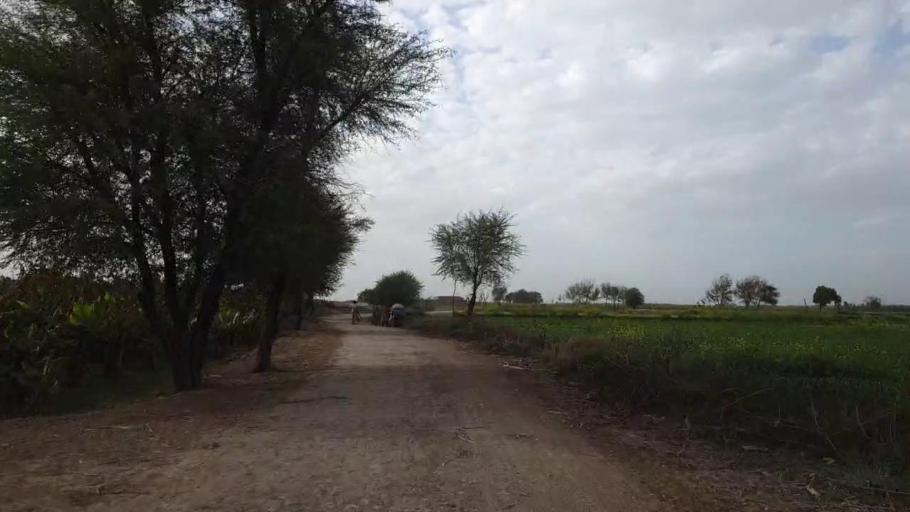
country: PK
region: Sindh
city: Tando Adam
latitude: 25.6554
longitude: 68.6070
